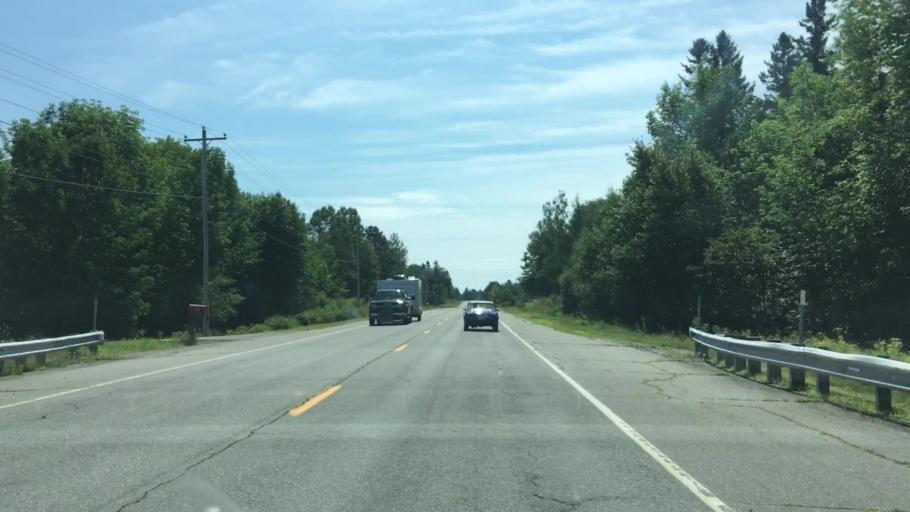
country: CA
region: New Brunswick
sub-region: Charlotte County
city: Saint Andrews
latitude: 45.0965
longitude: -67.1255
